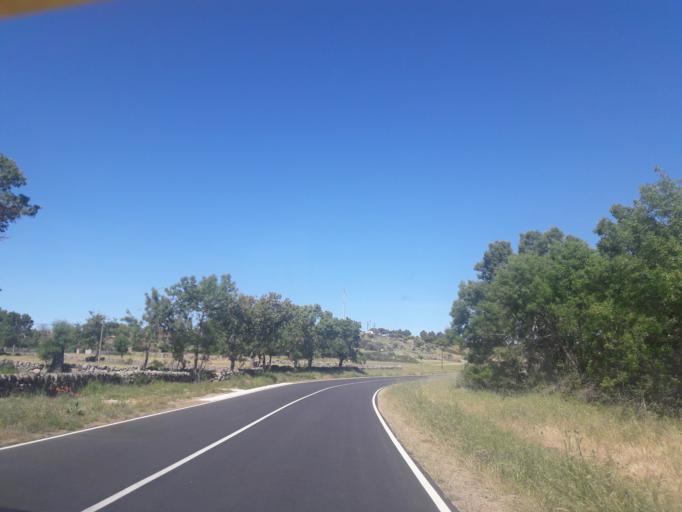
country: ES
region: Castille and Leon
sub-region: Provincia de Salamanca
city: Nava de Bejar
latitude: 40.4931
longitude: -5.6598
